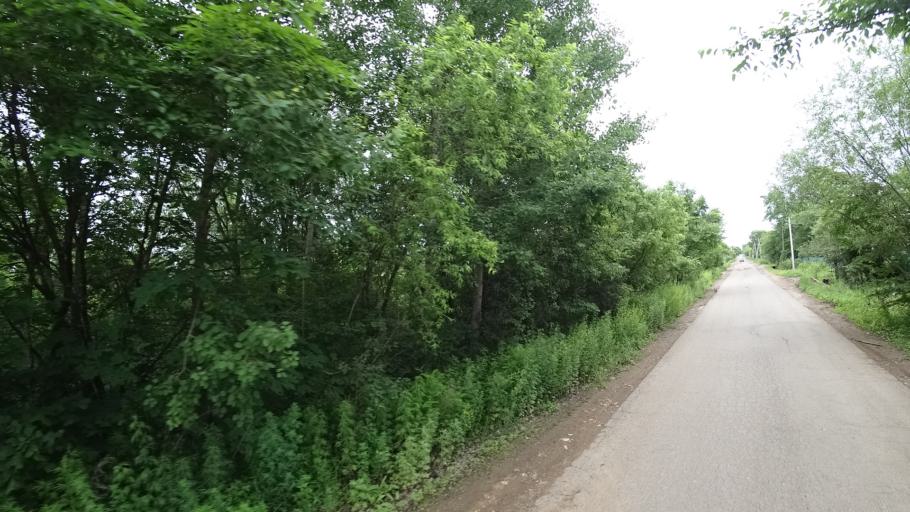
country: RU
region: Primorskiy
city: Novosysoyevka
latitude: 44.2063
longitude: 133.3291
